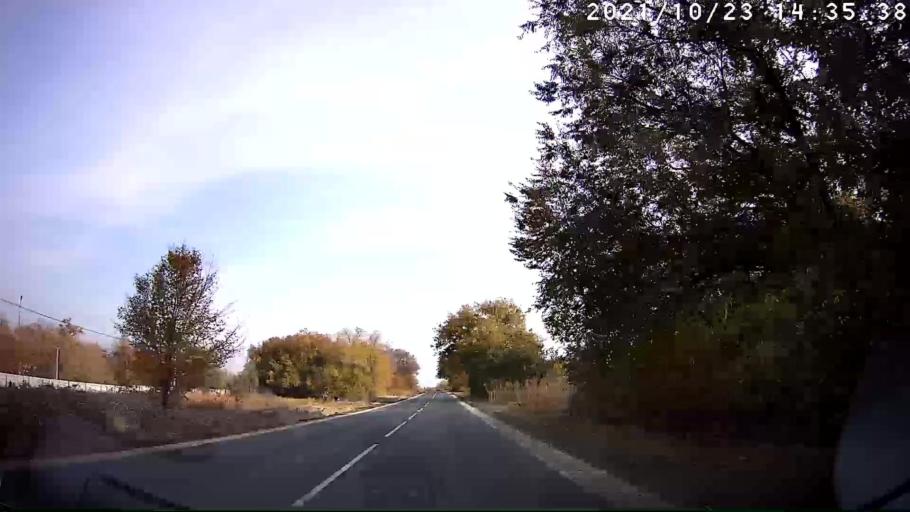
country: RU
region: Volgograd
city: Krasnoslobodsk
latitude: 48.5073
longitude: 44.5328
